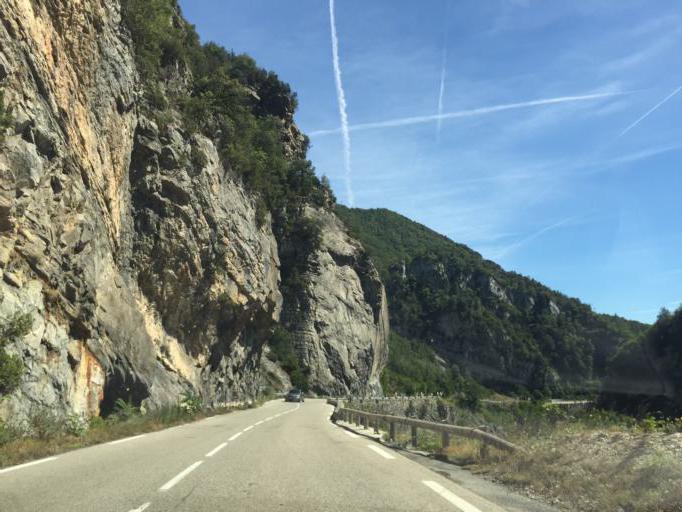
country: FR
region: Provence-Alpes-Cote d'Azur
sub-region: Departement des Alpes-Maritimes
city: Saint-Martin-Vesubie
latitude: 44.0504
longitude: 7.1276
